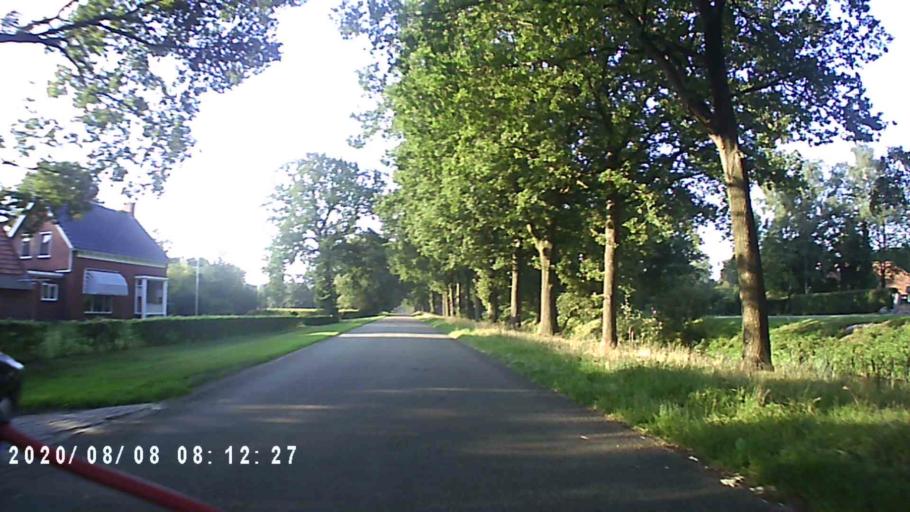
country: NL
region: Groningen
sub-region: Gemeente Leek
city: Leek
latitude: 53.1038
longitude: 6.3392
